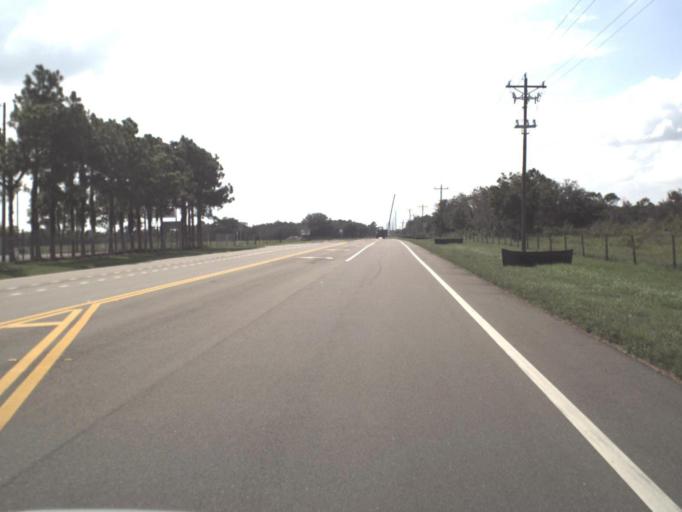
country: US
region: Florida
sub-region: Sarasota County
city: The Meadows
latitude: 27.4749
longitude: -82.3262
